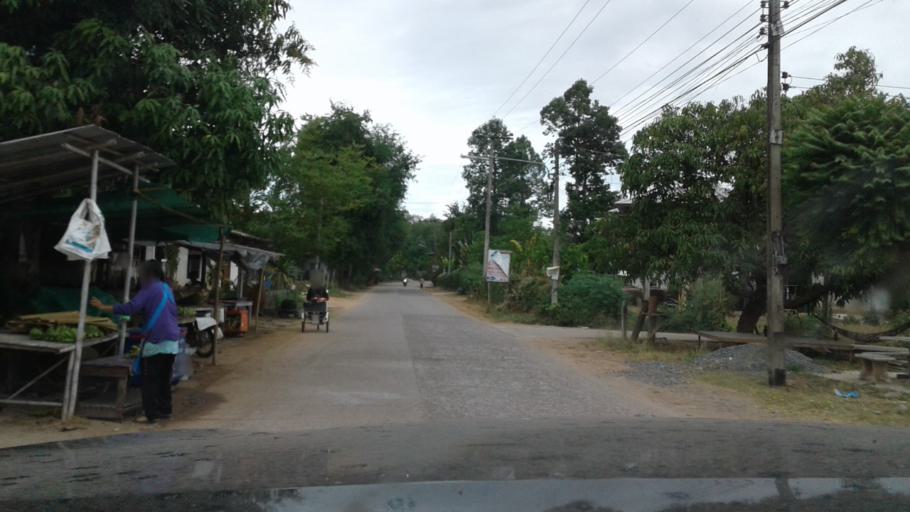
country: TH
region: Changwat Udon Thani
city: Nong Wua So
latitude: 17.2339
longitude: 102.5335
